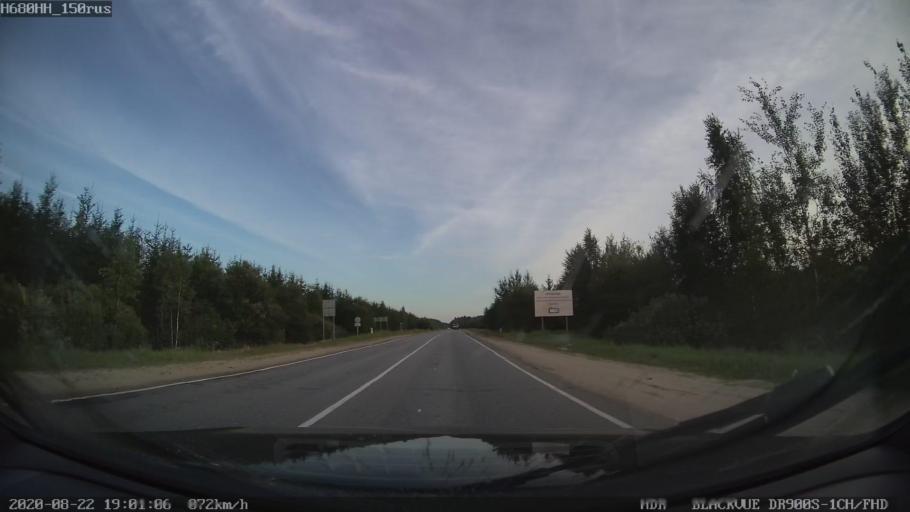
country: RU
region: Tverskaya
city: Vasil'yevskiy Mokh
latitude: 57.1228
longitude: 36.1132
